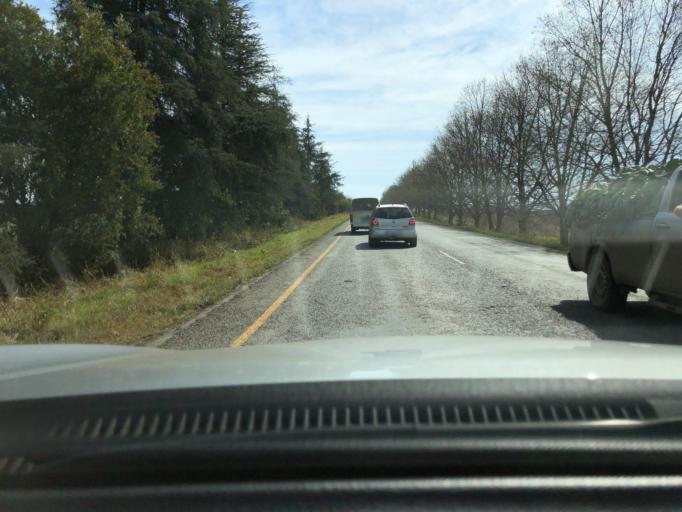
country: ZA
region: KwaZulu-Natal
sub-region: Sisonke District Municipality
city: Ixopo
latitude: -30.1295
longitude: 30.0814
